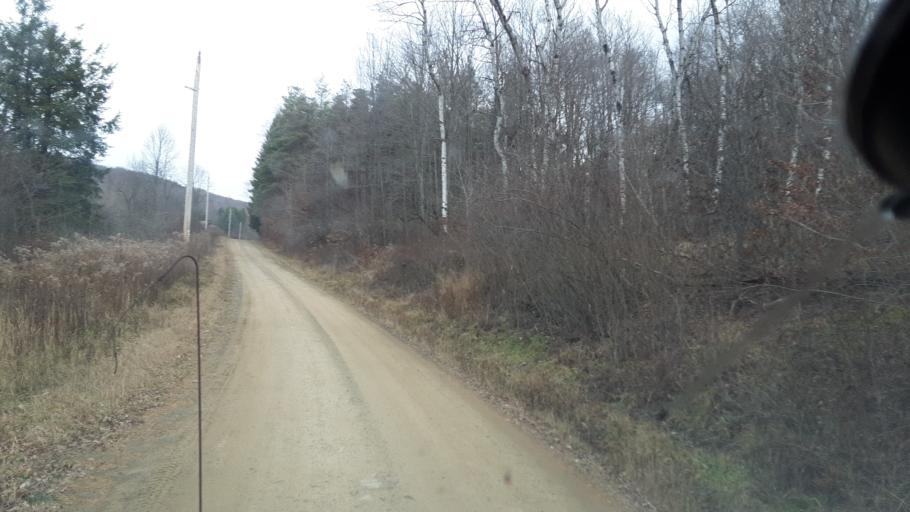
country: US
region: Pennsylvania
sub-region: Tioga County
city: Westfield
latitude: 41.9094
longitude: -77.7082
